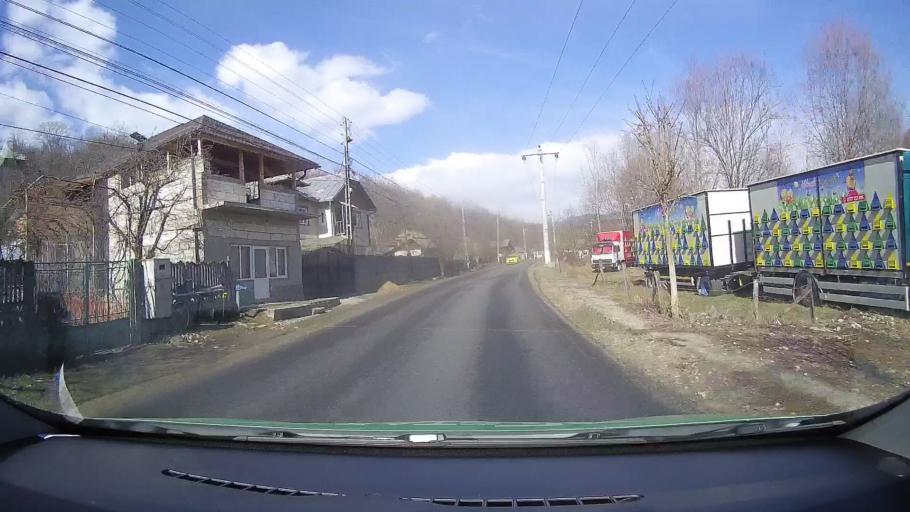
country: RO
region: Dambovita
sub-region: Comuna Runcu
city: Badeni
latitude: 45.1638
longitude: 25.3959
